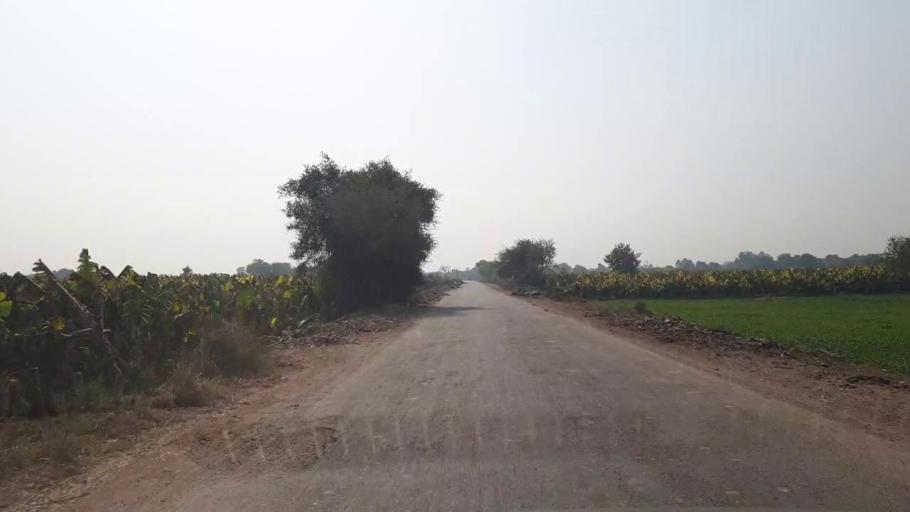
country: PK
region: Sindh
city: Hala
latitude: 25.8669
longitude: 68.4297
